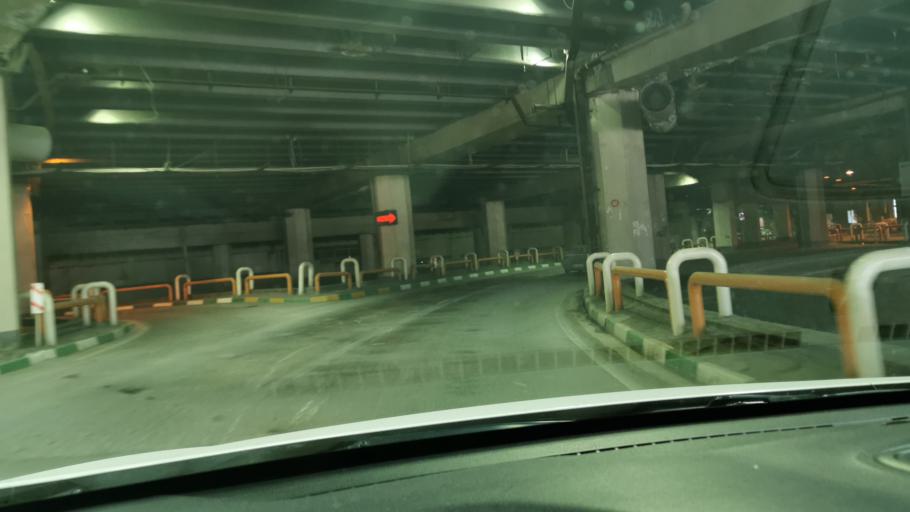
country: IR
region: Razavi Khorasan
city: Mashhad
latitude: 36.2896
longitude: 59.6181
